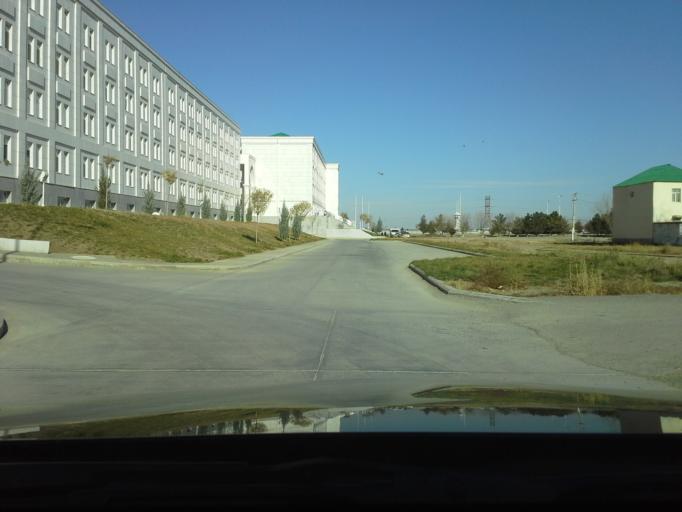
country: TM
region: Ahal
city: Ashgabat
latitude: 37.9745
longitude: 58.3429
